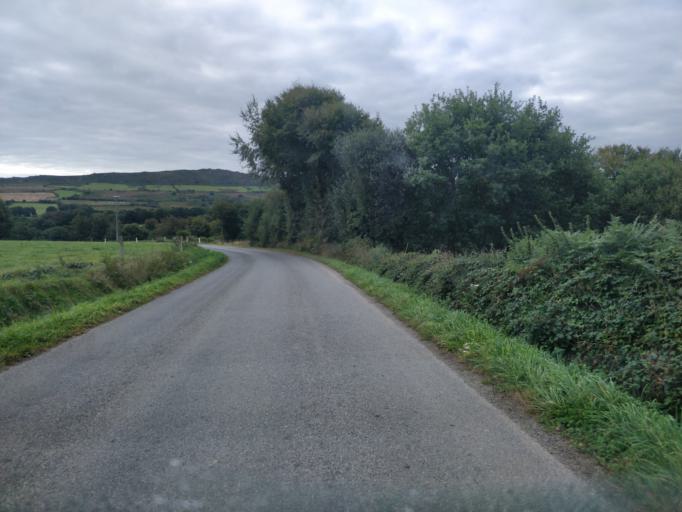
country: FR
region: Brittany
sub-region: Departement du Finistere
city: Plouneour-Menez
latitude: 48.4445
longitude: -3.8486
